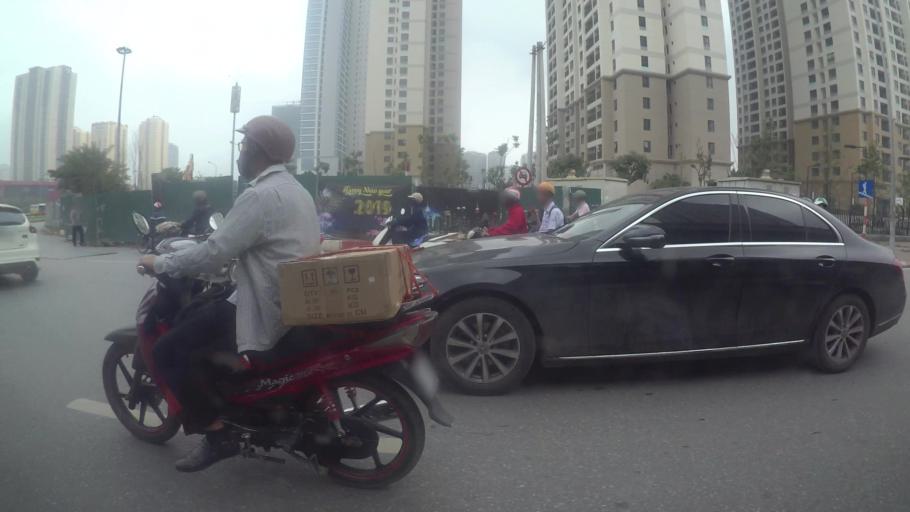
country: VN
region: Ha Noi
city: Thanh Xuan
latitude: 21.0043
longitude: 105.7933
